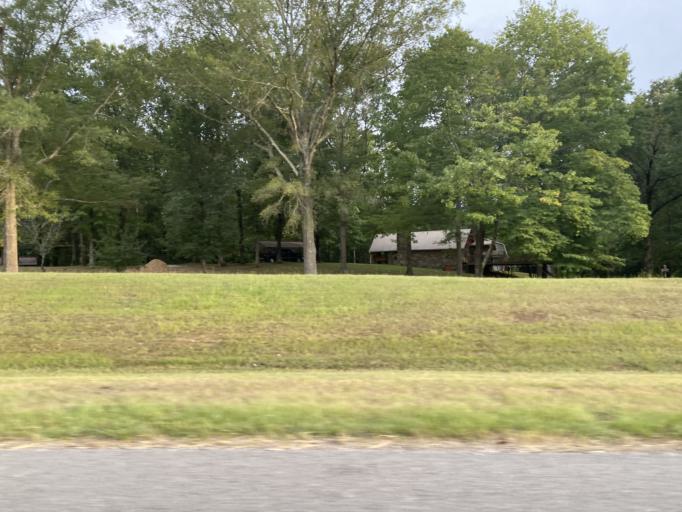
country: US
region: Alabama
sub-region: Franklin County
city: Red Bay
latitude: 34.4492
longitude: -88.0569
